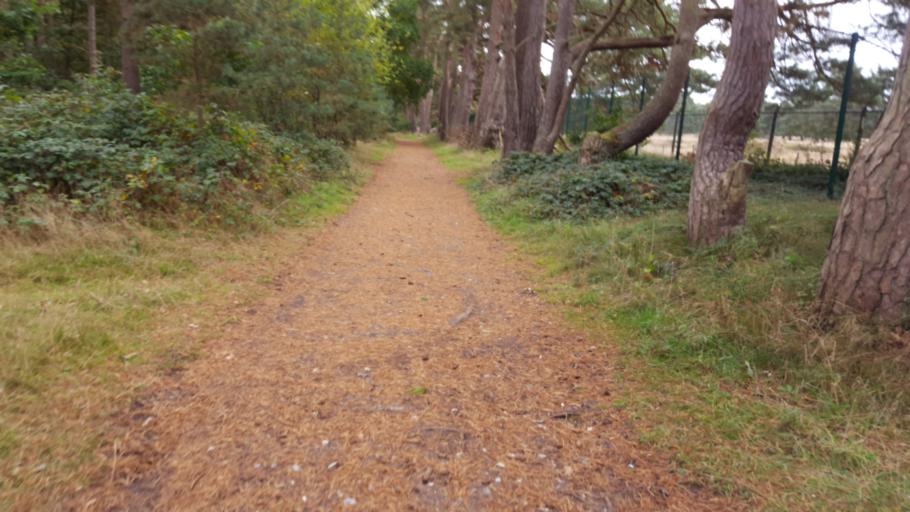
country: GB
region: England
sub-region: Norfolk
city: Weeting
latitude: 52.3916
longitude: 0.6310
